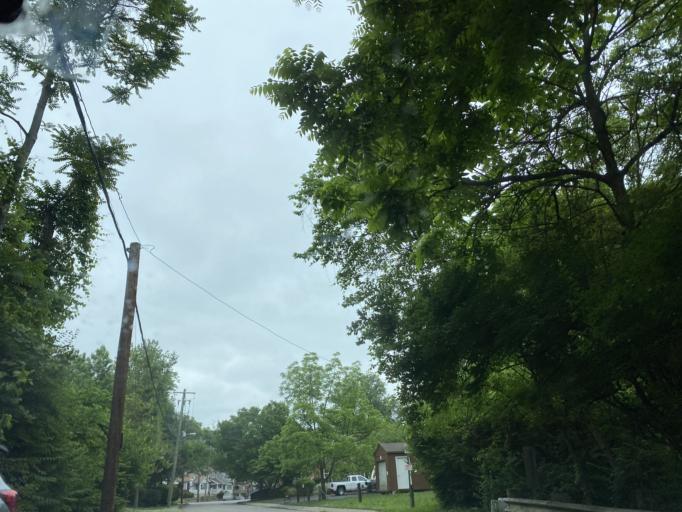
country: US
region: Kentucky
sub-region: Campbell County
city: Bellevue
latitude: 39.0991
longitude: -84.4787
